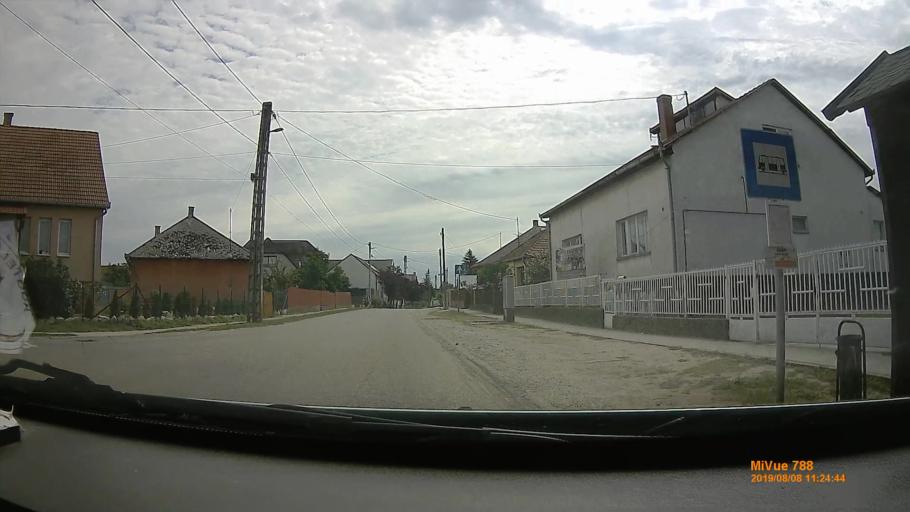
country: HU
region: Szabolcs-Szatmar-Bereg
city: Balkany
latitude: 47.7704
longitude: 21.8564
